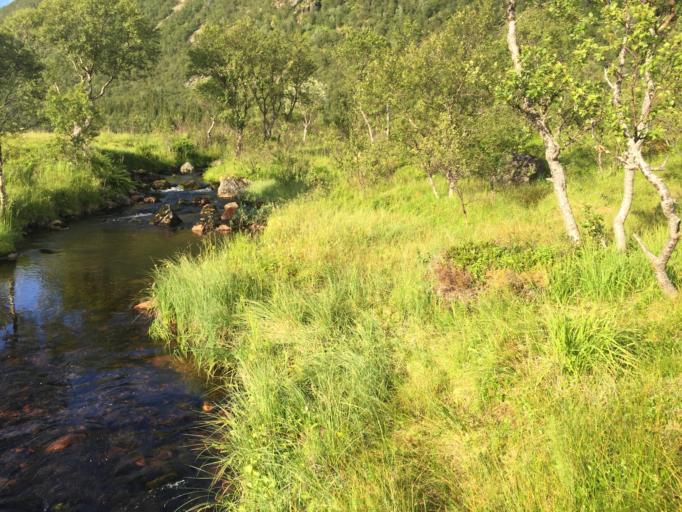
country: NO
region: Nordland
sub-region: Vagan
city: Kabelvag
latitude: 68.3009
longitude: 14.4308
